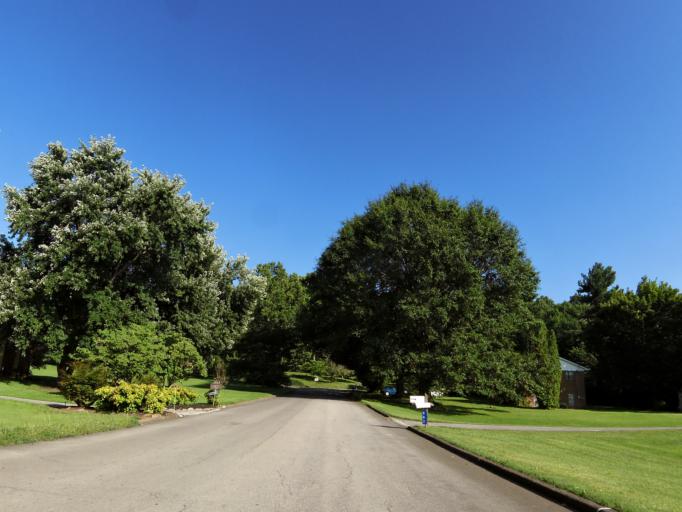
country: US
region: Tennessee
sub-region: Blount County
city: Eagleton Village
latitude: 35.7957
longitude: -83.9328
